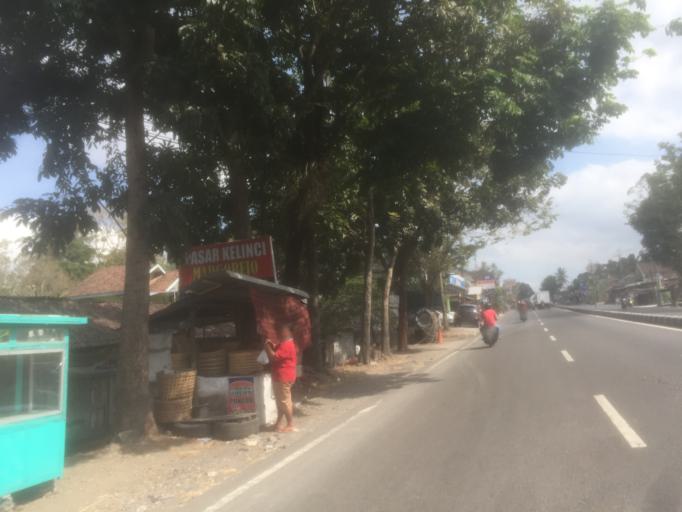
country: ID
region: Daerah Istimewa Yogyakarta
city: Sleman
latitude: -7.6693
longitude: 110.3334
